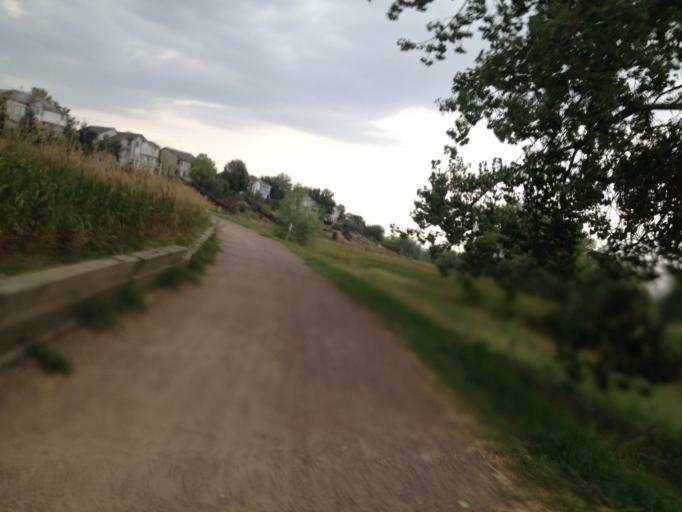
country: US
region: Colorado
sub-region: Boulder County
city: Louisville
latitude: 39.9824
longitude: -105.1520
